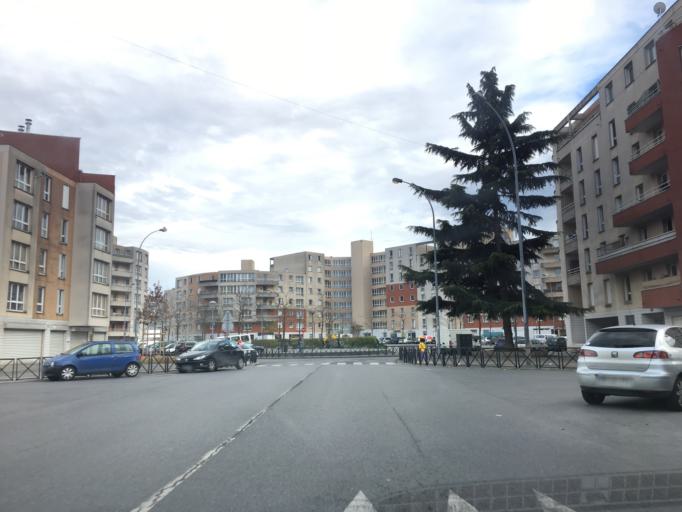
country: FR
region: Ile-de-France
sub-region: Departement du Val-de-Marne
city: Bonneuil-sur-Marne
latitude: 48.7654
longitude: 2.4859
